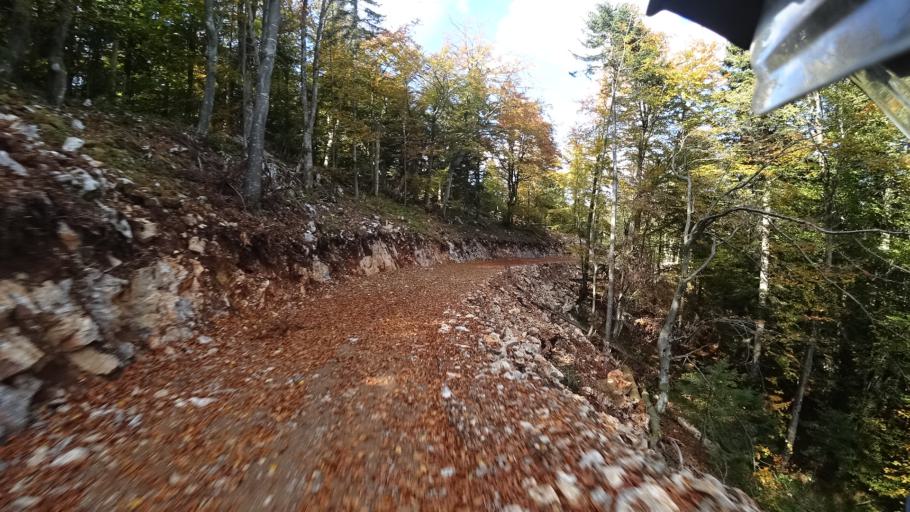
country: HR
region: Karlovacka
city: Plaski
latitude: 45.0582
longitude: 15.3550
